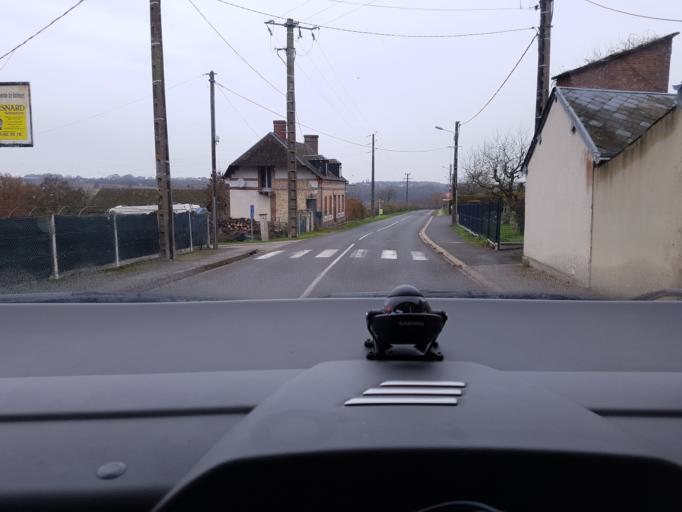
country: FR
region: Haute-Normandie
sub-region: Departement de l'Eure
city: Rugles
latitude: 48.9099
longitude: 0.7482
